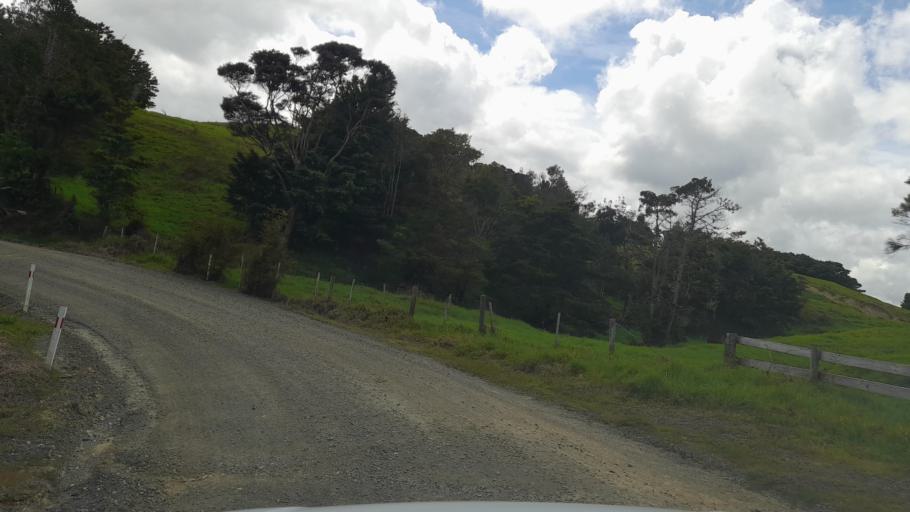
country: NZ
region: Auckland
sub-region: Auckland
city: Wellsford
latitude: -36.2077
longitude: 174.3355
